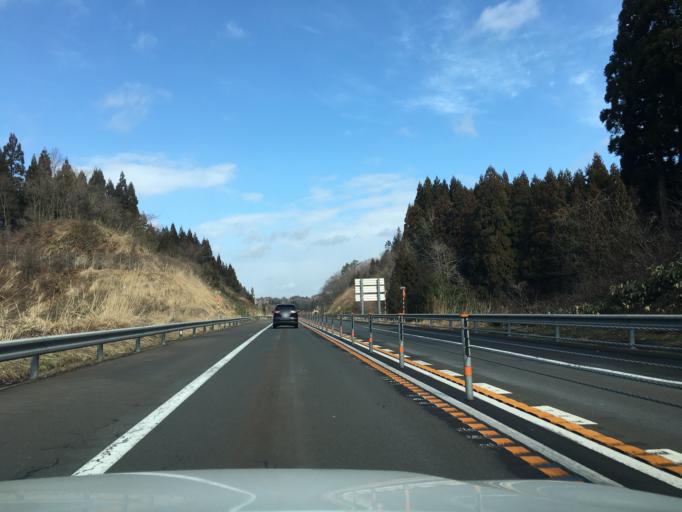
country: JP
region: Akita
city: Akita
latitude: 39.7084
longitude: 140.1841
